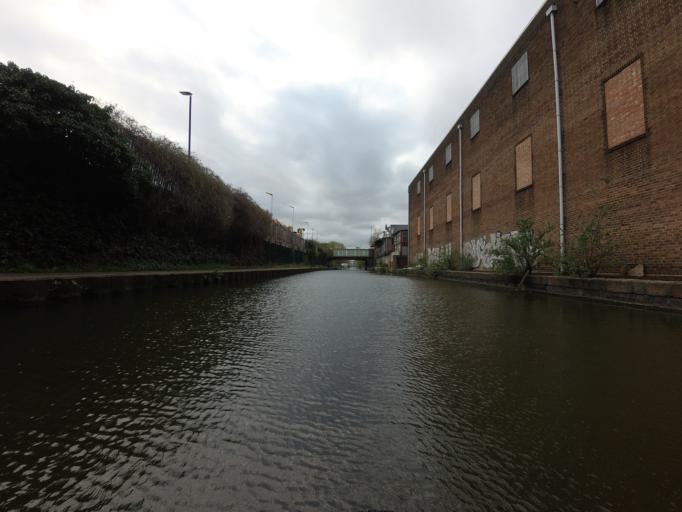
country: GB
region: England
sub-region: Greater London
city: Acton
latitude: 51.5340
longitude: -0.2592
